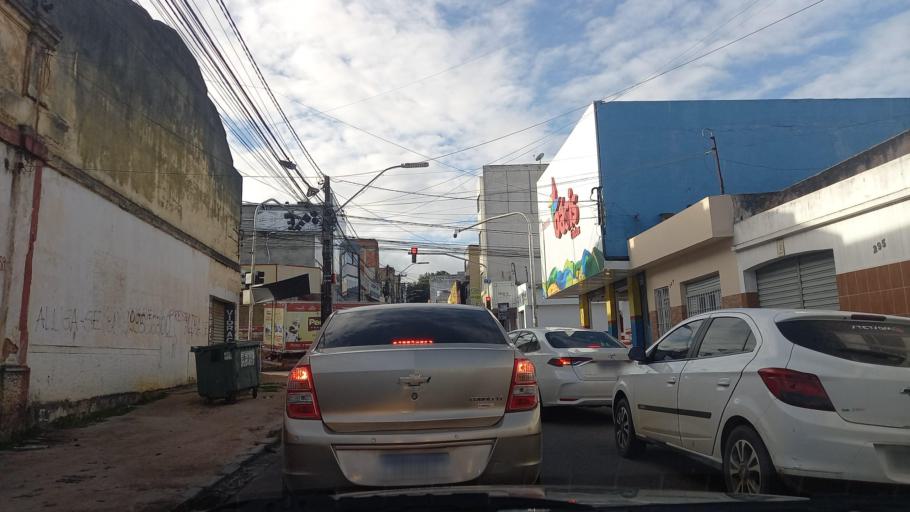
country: BR
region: Pernambuco
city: Garanhuns
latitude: -8.8939
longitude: -36.4951
